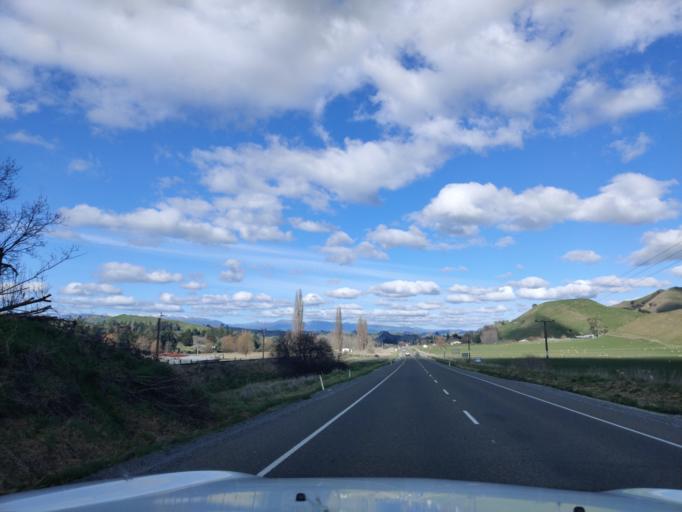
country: NZ
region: Manawatu-Wanganui
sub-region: Ruapehu District
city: Waiouru
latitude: -39.6987
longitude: 175.8264
